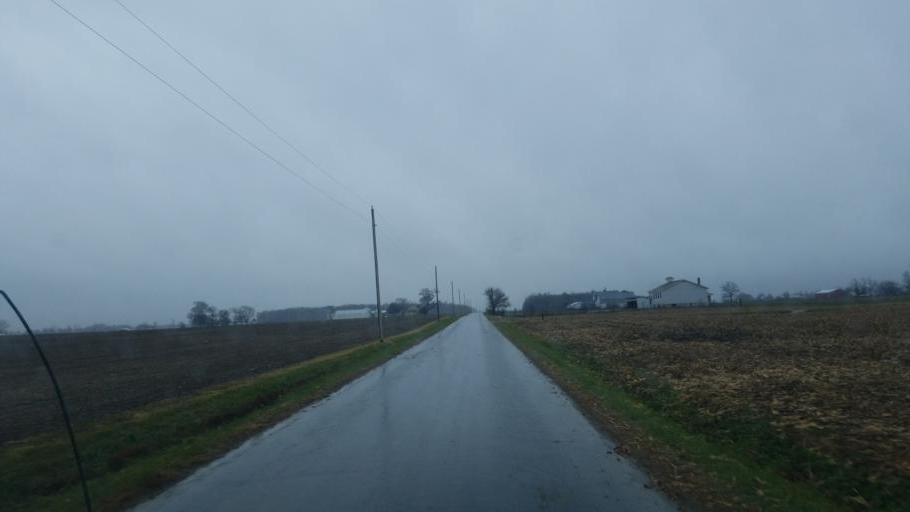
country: US
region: Indiana
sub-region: Adams County
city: Berne
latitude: 40.6199
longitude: -84.8783
